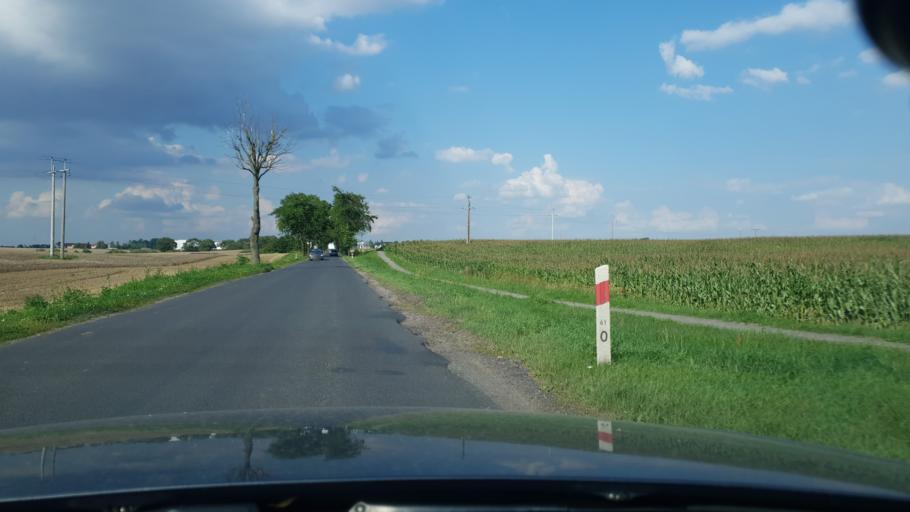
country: PL
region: Kujawsko-Pomorskie
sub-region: Powiat wabrzeski
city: Wabrzezno
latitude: 53.2679
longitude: 18.9104
